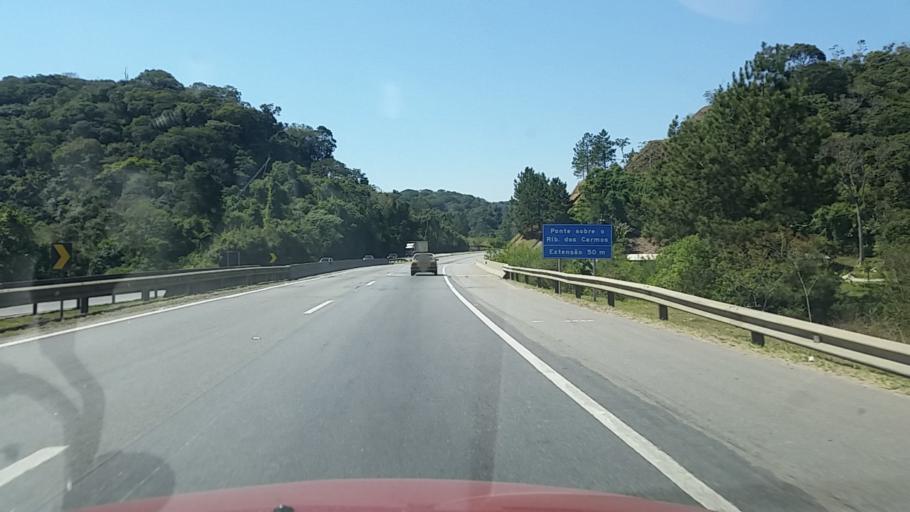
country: BR
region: Sao Paulo
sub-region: Juquitiba
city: Juquitiba
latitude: -23.9436
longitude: -47.0960
